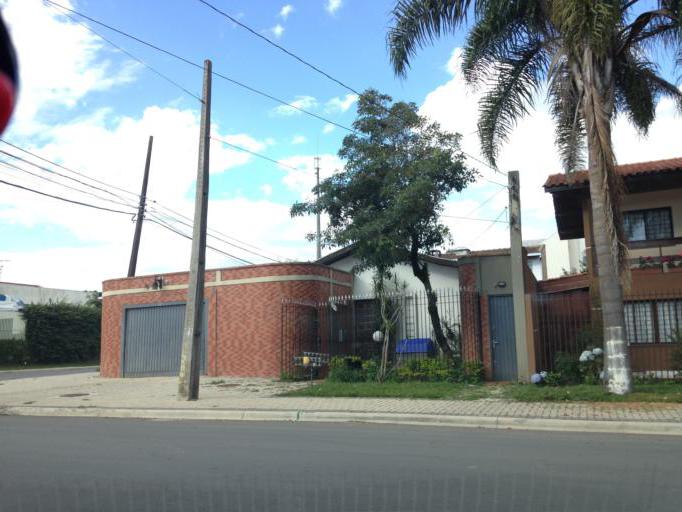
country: BR
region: Parana
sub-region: Pinhais
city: Pinhais
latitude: -25.4132
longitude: -49.2246
